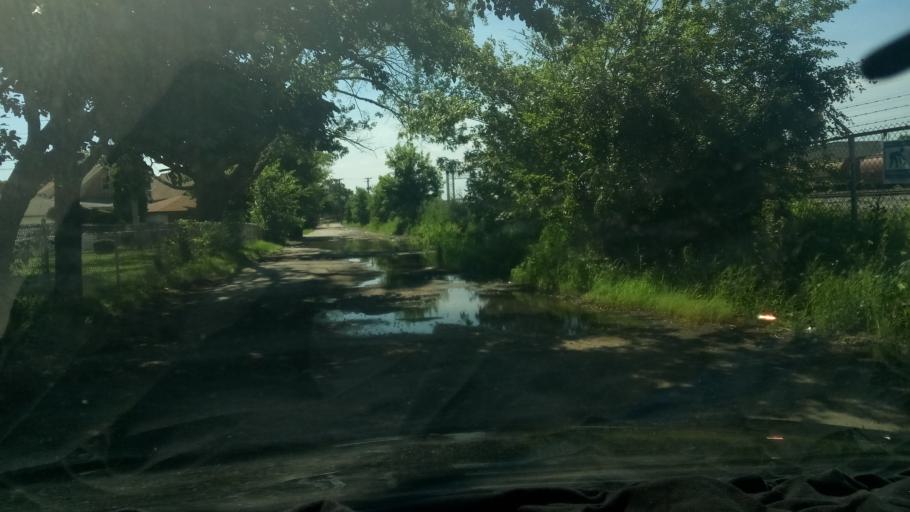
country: US
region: Illinois
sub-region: Cook County
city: Hometown
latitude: 41.7621
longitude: -87.7207
